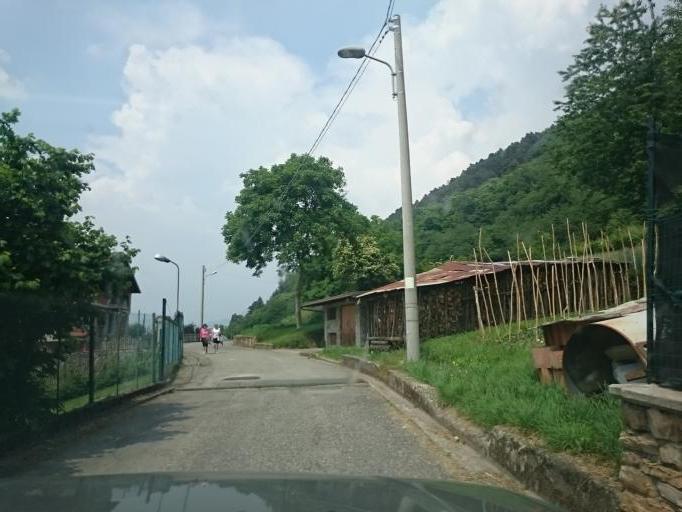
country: IT
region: Lombardy
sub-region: Provincia di Brescia
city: Paspardo
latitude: 46.0355
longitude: 10.3672
